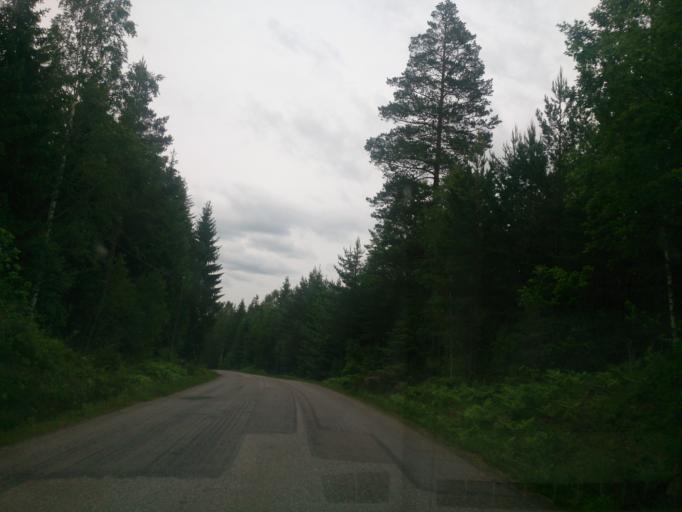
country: SE
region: OEstergoetland
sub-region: Soderkopings Kommun
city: Soederkoeping
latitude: 58.2865
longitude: 16.2395
